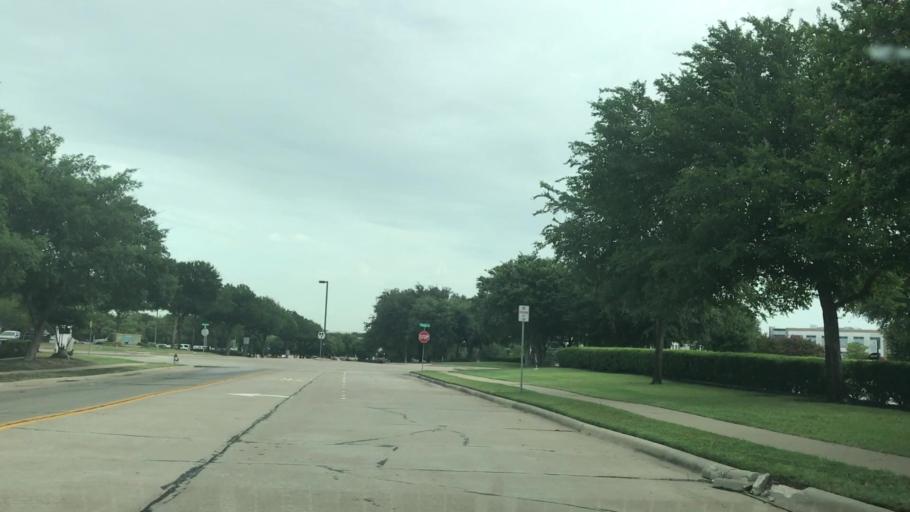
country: US
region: Texas
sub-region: Dallas County
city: Coppell
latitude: 32.9200
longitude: -97.0026
